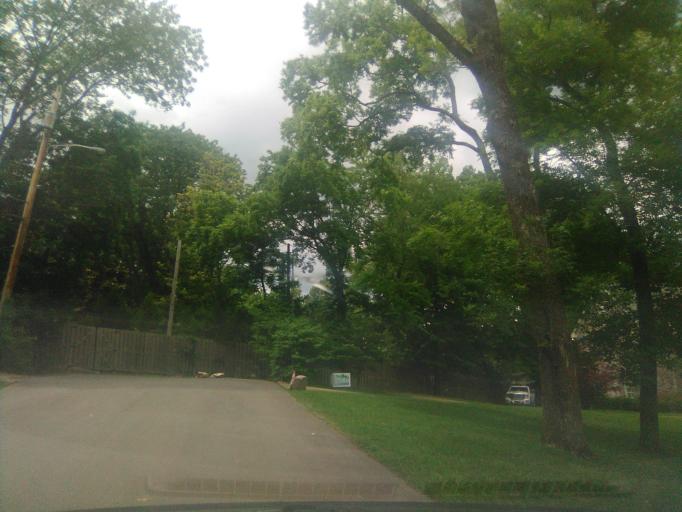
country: US
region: Tennessee
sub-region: Davidson County
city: Belle Meade
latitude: 36.0892
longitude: -86.8739
